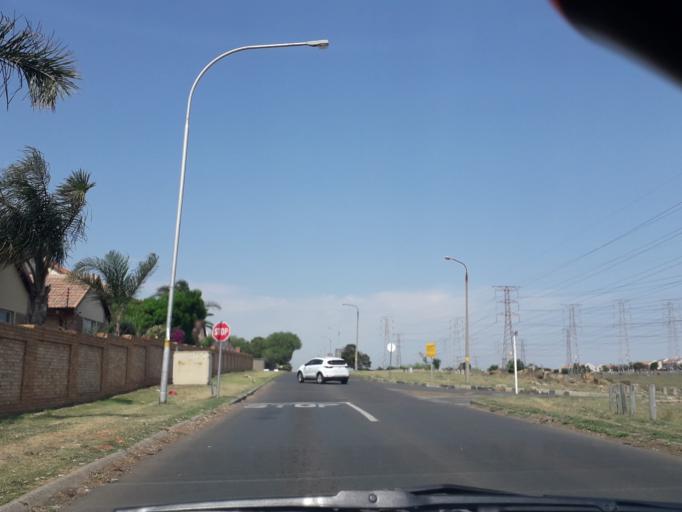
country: ZA
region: Gauteng
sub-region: City of Johannesburg Metropolitan Municipality
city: Modderfontein
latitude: -26.1219
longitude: 28.1650
